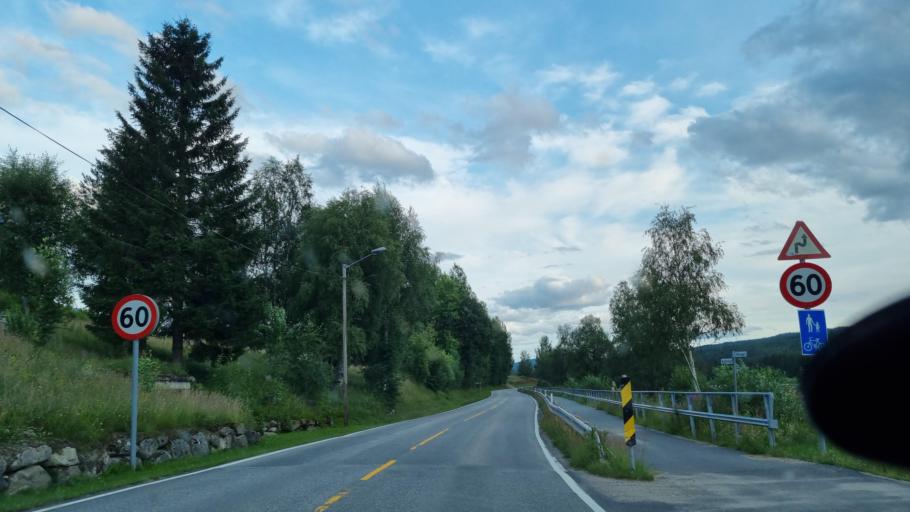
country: NO
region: Hedmark
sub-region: Trysil
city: Innbygda
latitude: 61.3087
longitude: 12.2725
